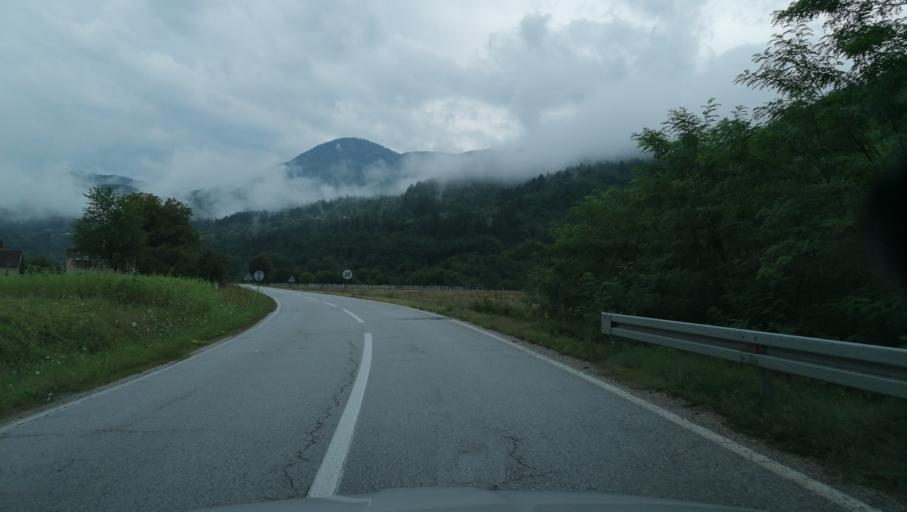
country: RS
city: Durici
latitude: 43.7634
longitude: 19.3871
